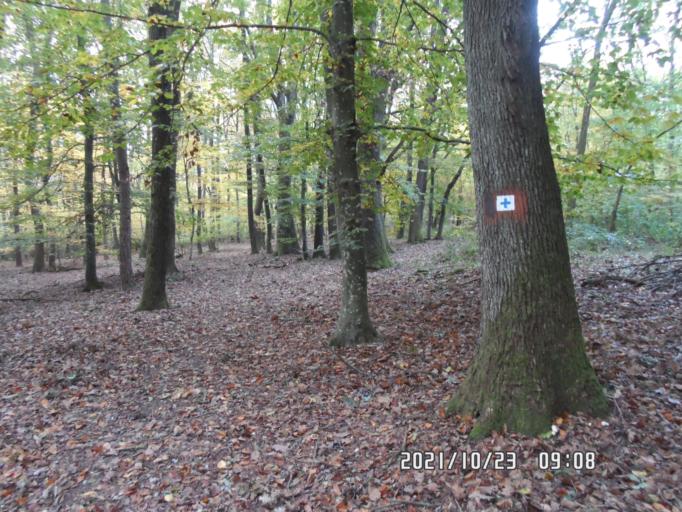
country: SI
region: Kobilje
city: Kobilje
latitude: 46.7239
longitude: 16.3717
